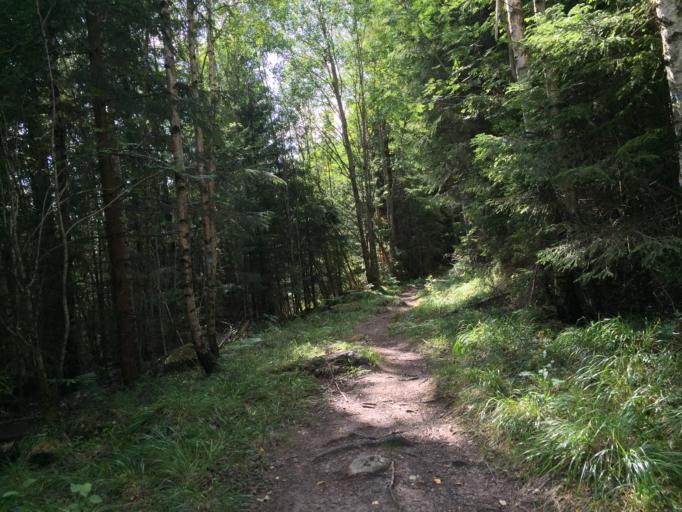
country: NO
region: Akershus
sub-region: Raelingen
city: Fjerdingby
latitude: 59.9116
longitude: 11.0368
